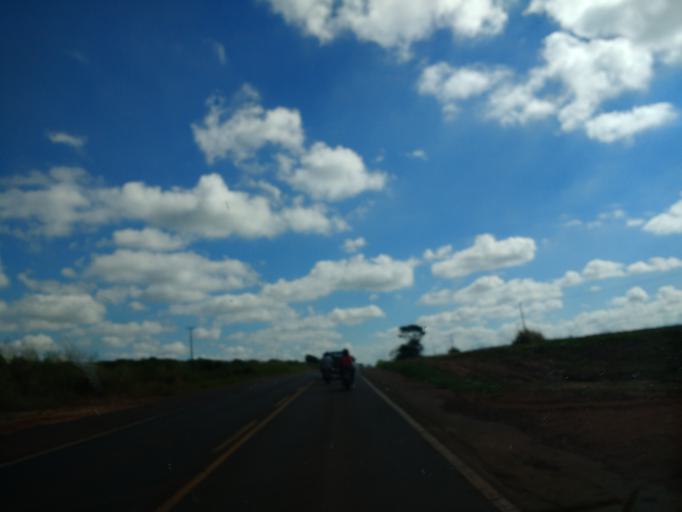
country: BR
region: Parana
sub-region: Alto Piquiri
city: Alto Piquiri
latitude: -23.8928
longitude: -53.4503
